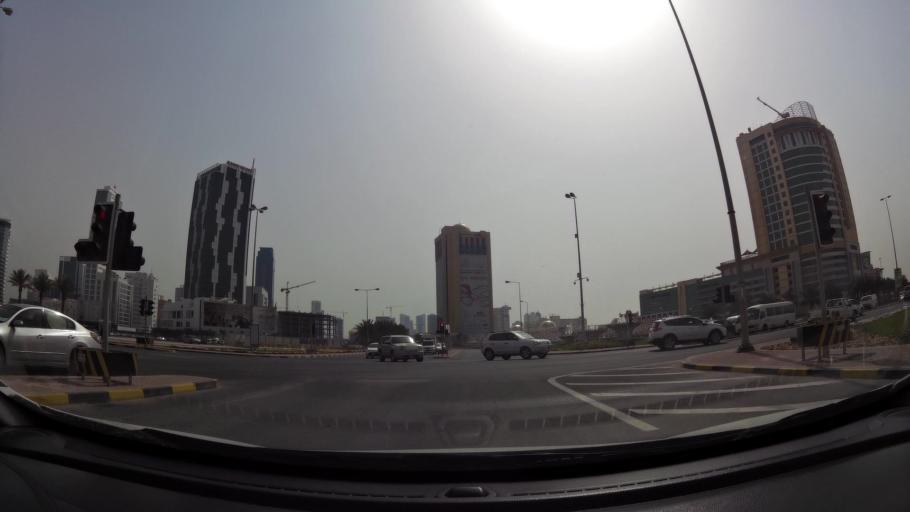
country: BH
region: Manama
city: Jidd Hafs
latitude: 26.2349
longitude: 50.5337
